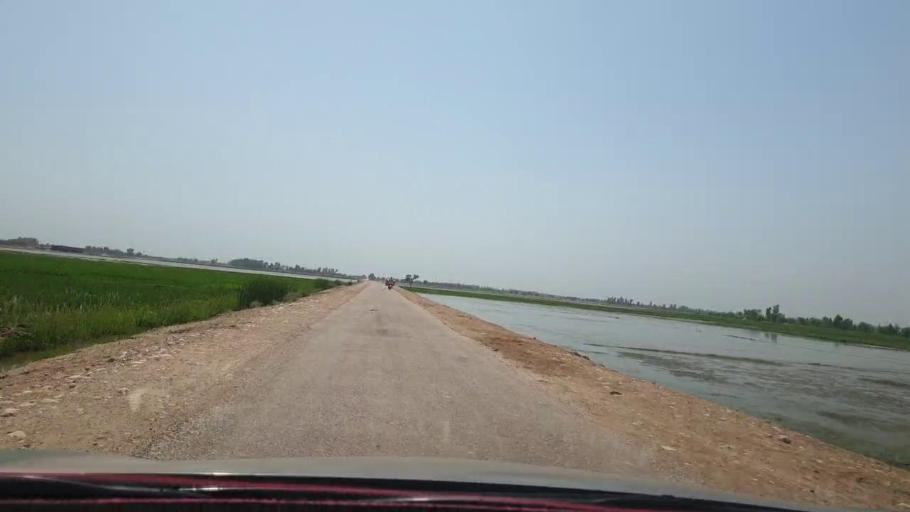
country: PK
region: Sindh
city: Warah
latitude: 27.5509
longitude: 67.7958
